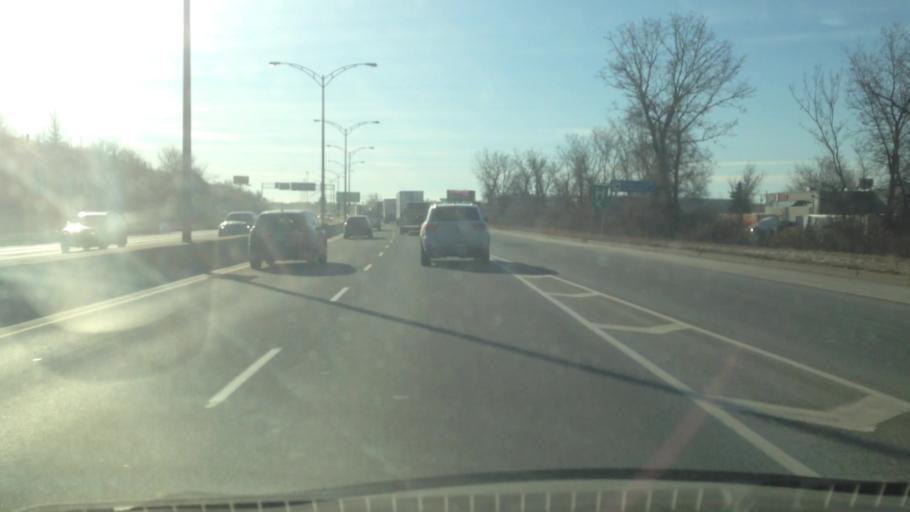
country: CA
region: Quebec
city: Cote-Saint-Luc
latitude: 45.4580
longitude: -73.6972
